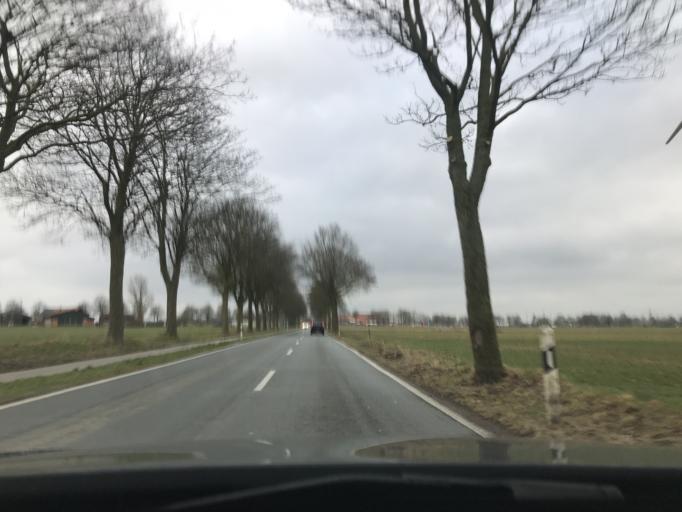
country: DE
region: North Rhine-Westphalia
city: Kalkar
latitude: 51.7088
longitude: 6.2306
